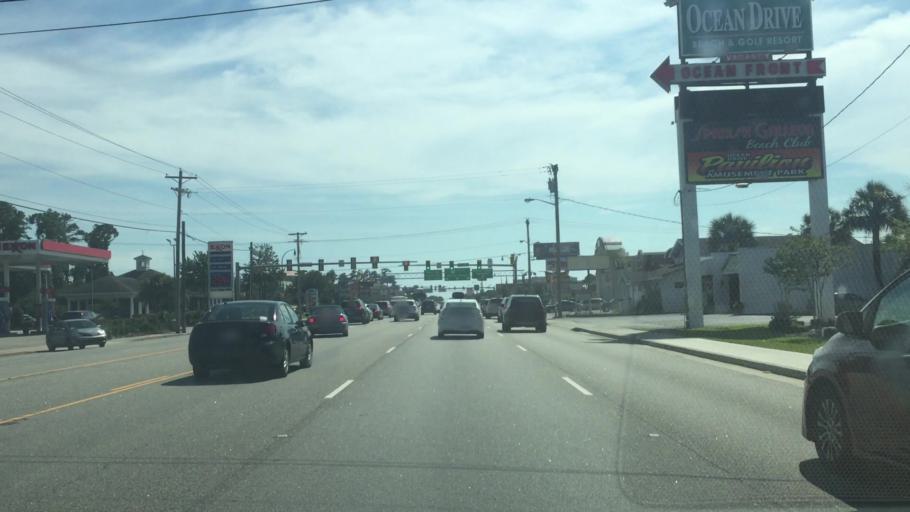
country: US
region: South Carolina
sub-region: Horry County
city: North Myrtle Beach
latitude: 33.8305
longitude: -78.6773
